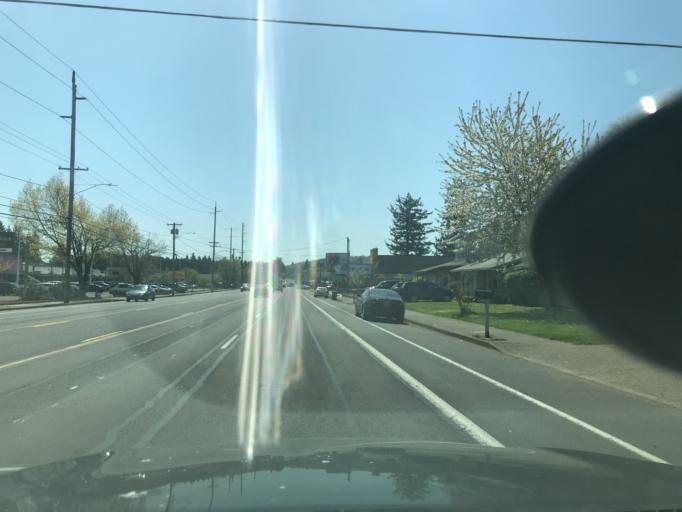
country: US
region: Oregon
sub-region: Multnomah County
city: Gresham
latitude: 45.5067
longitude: -122.4758
